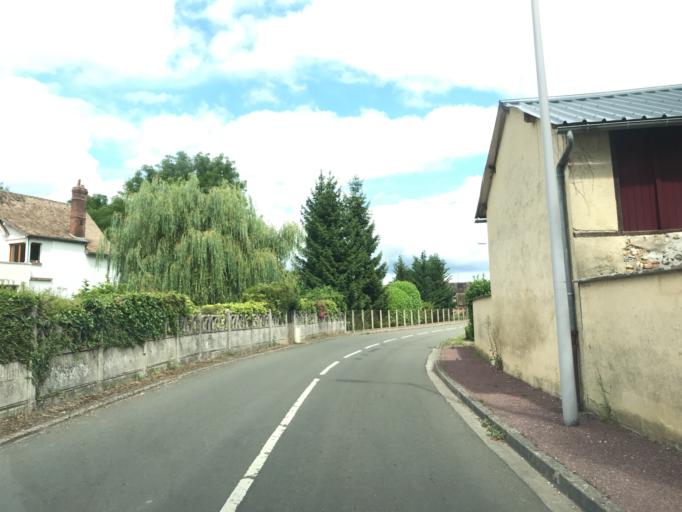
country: FR
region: Haute-Normandie
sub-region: Departement de l'Eure
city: Houlbec-Cocherel
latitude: 49.0641
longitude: 1.2943
